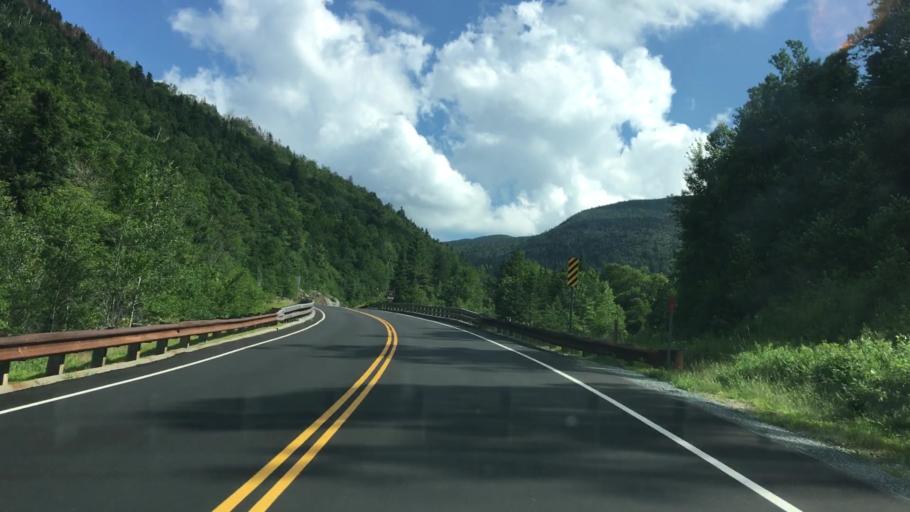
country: US
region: New Hampshire
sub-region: Grafton County
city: Woodstock
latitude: 44.0460
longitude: -71.7930
